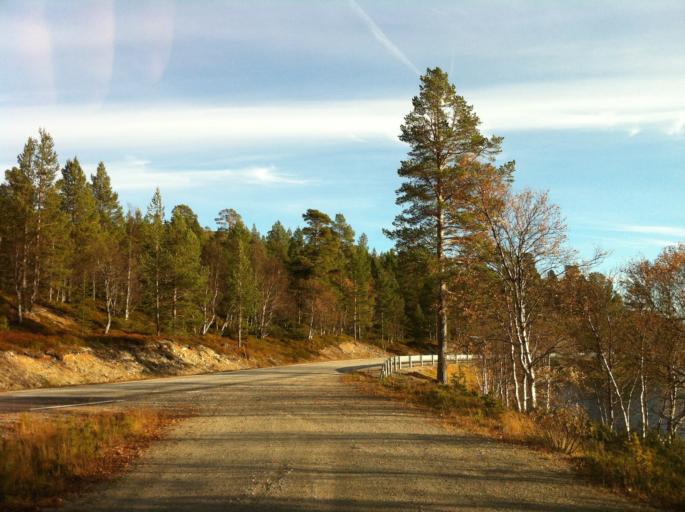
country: NO
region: Hedmark
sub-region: Engerdal
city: Engerdal
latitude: 62.1088
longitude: 12.0192
